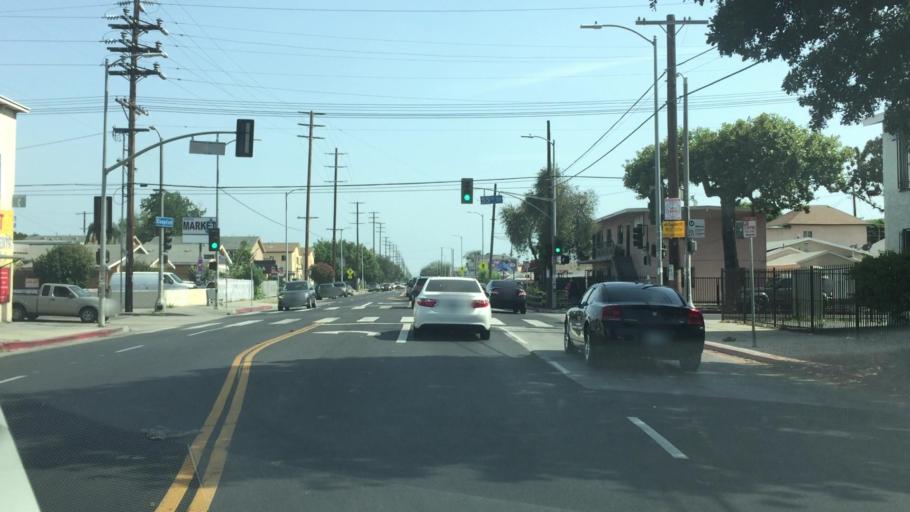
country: US
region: California
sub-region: Los Angeles County
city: Huntington Park
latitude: 33.9934
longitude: -118.2478
